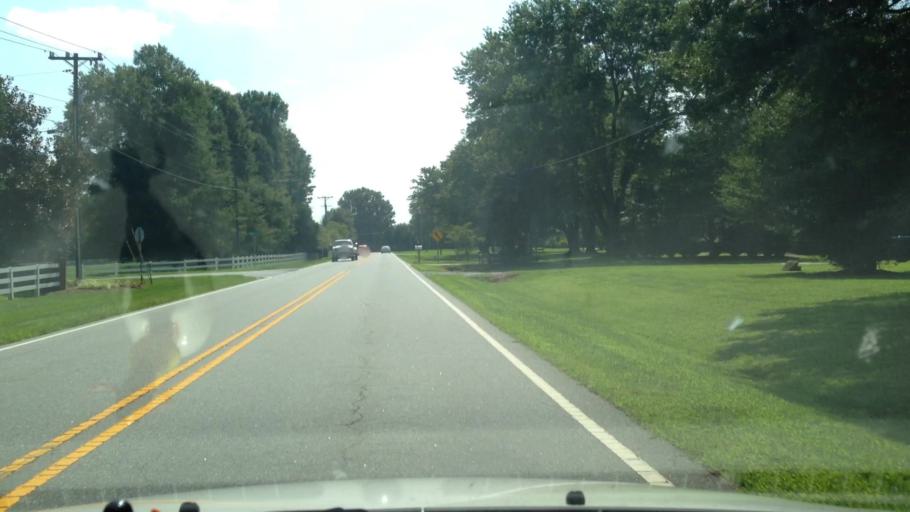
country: US
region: North Carolina
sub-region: Guilford County
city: Oak Ridge
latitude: 36.1657
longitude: -80.0006
